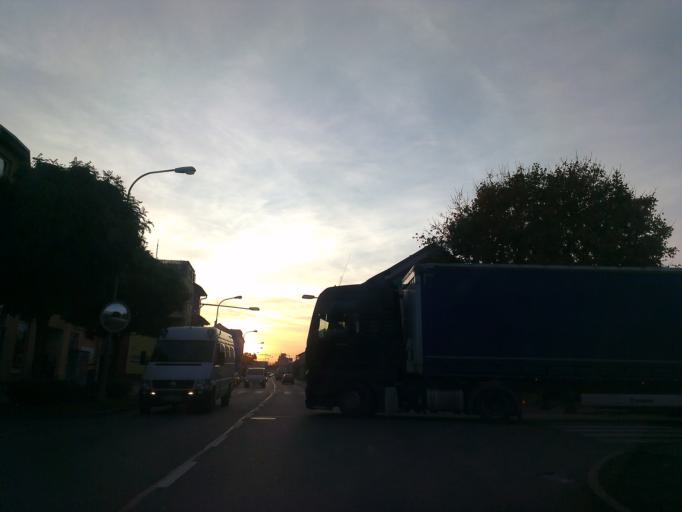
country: CZ
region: South Moravian
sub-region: Mesto Brno
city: Brno
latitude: 49.1652
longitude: 16.6127
